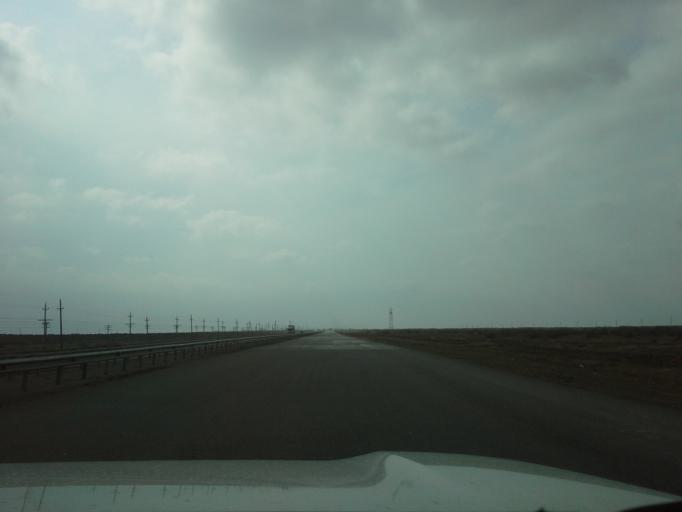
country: IR
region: Razavi Khorasan
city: Kalat-e Naderi
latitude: 37.2077
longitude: 60.0607
